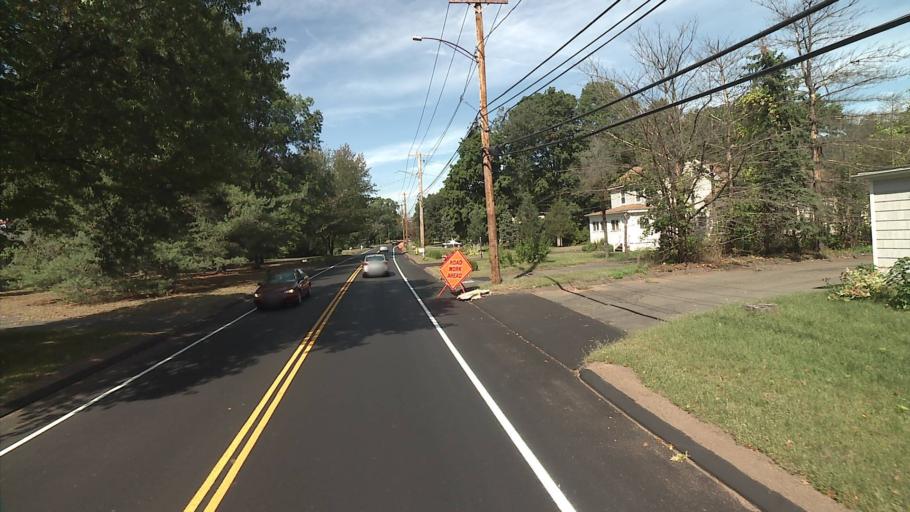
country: US
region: Connecticut
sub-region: New Haven County
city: North Haven
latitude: 41.3783
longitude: -72.8567
